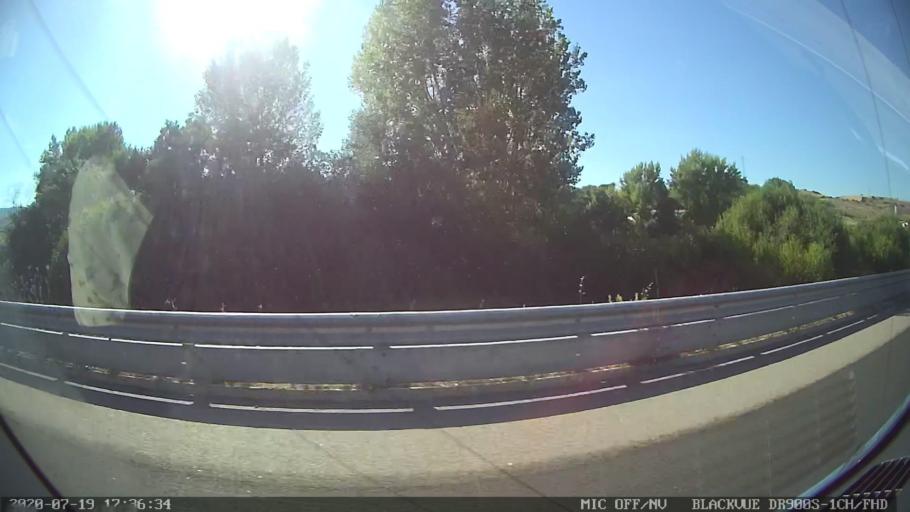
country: PT
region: Braganca
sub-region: Braganca Municipality
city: Braganca
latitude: 41.7491
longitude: -6.8081
